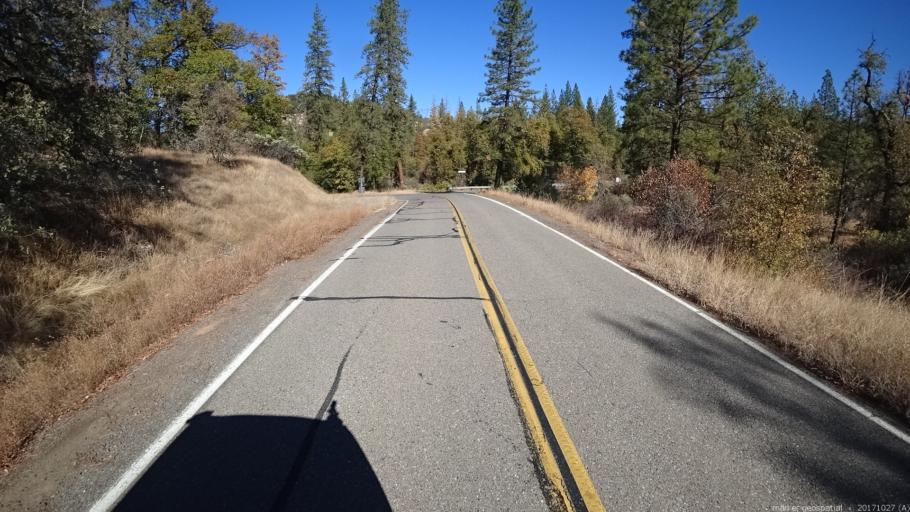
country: US
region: California
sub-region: Shasta County
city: Bella Vista
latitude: 40.7373
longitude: -122.0072
